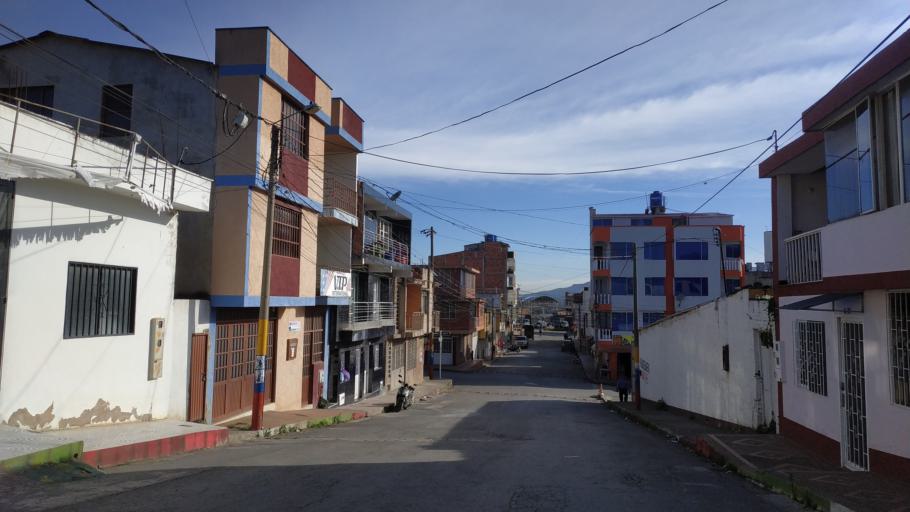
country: CO
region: Santander
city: Barbosa
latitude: 5.9356
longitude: -73.6125
